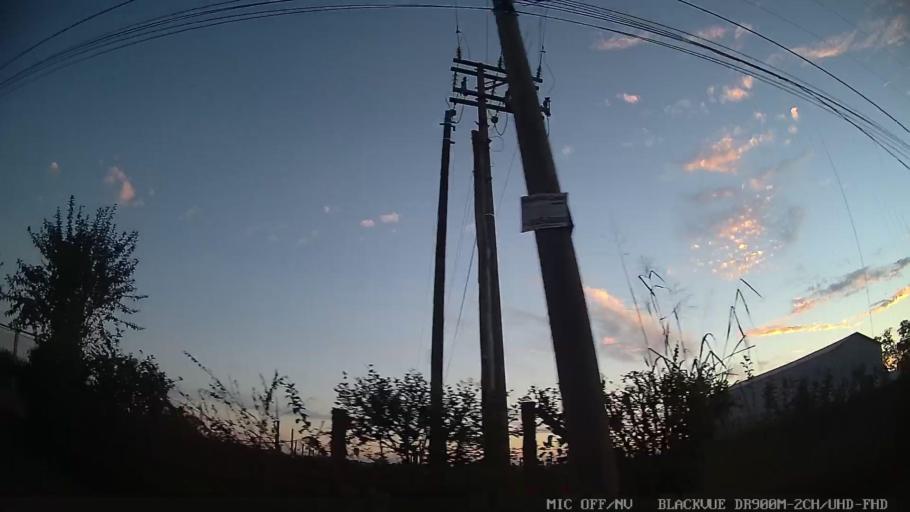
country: BR
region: Sao Paulo
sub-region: Indaiatuba
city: Indaiatuba
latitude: -23.1418
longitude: -47.1604
